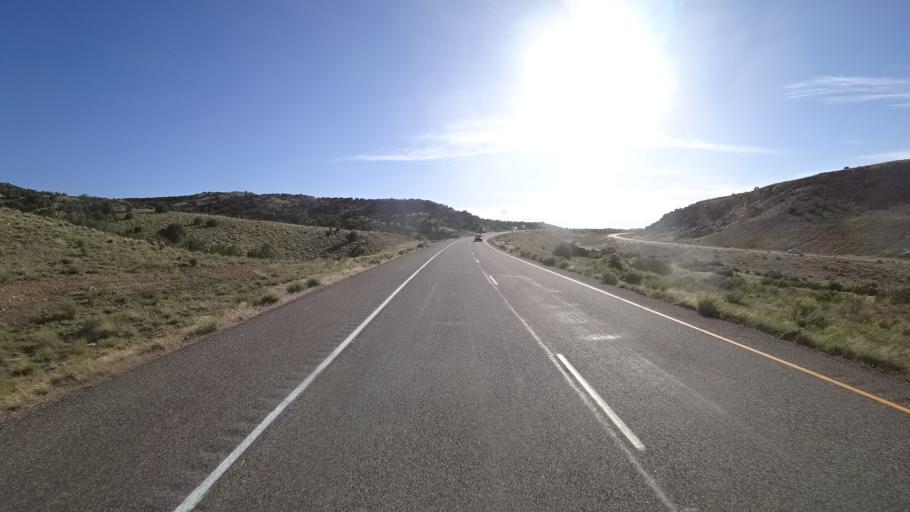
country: US
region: Colorado
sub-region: Mesa County
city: Loma
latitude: 39.1878
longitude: -109.0305
